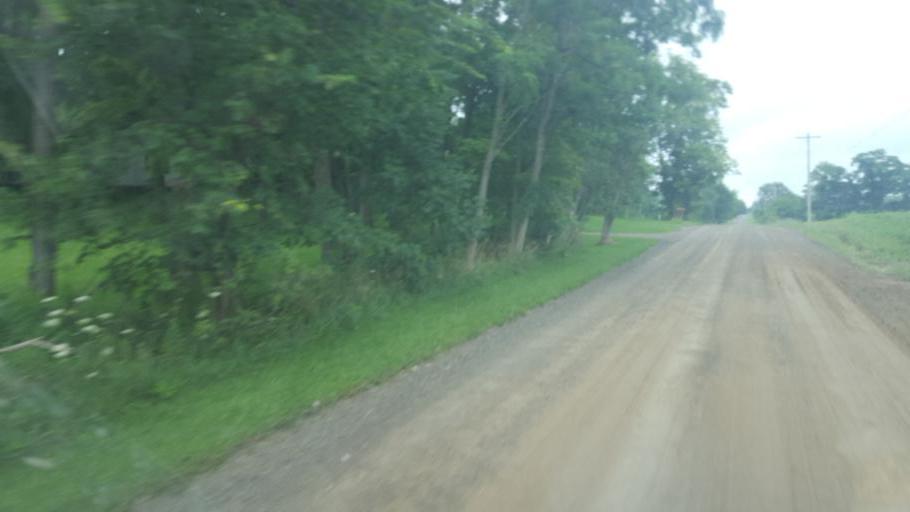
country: US
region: Ohio
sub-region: Morrow County
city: Mount Gilead
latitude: 40.4232
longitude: -82.7724
